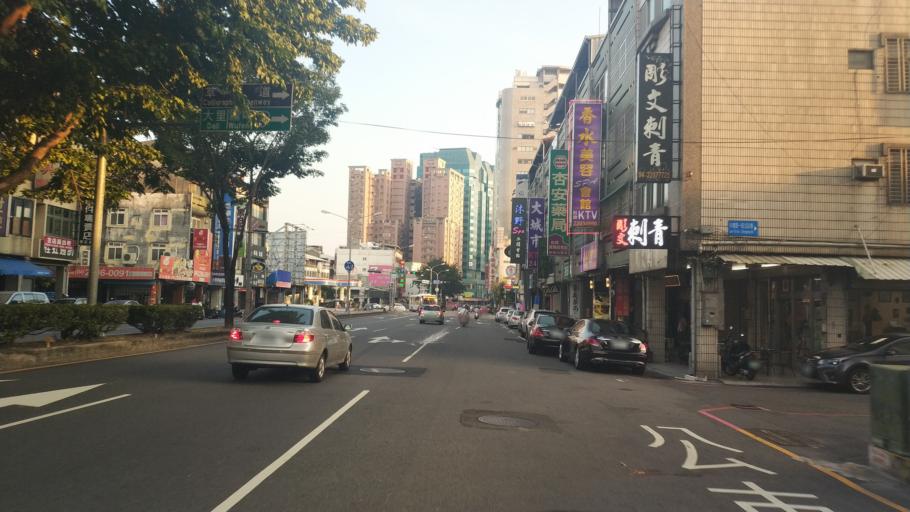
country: TW
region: Taiwan
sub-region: Taichung City
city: Taichung
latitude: 24.1568
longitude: 120.6765
